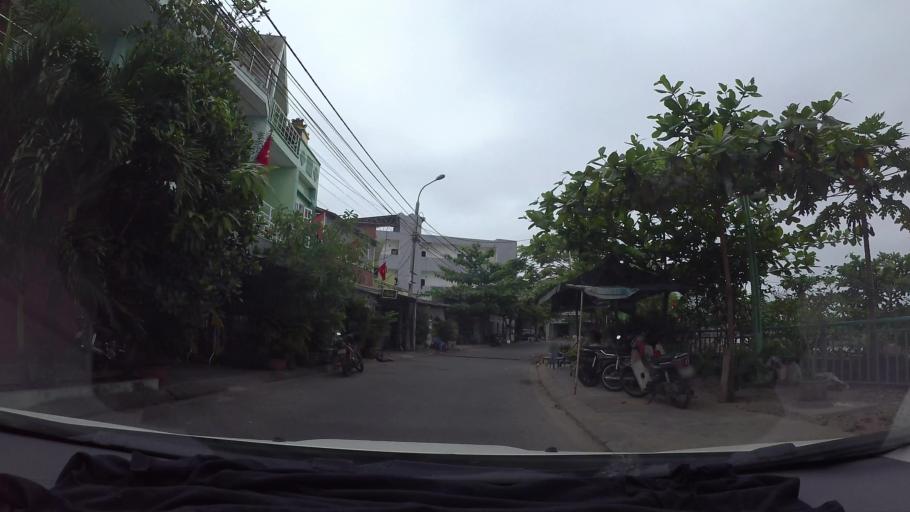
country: VN
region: Da Nang
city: Thanh Khe
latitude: 16.0745
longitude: 108.1779
